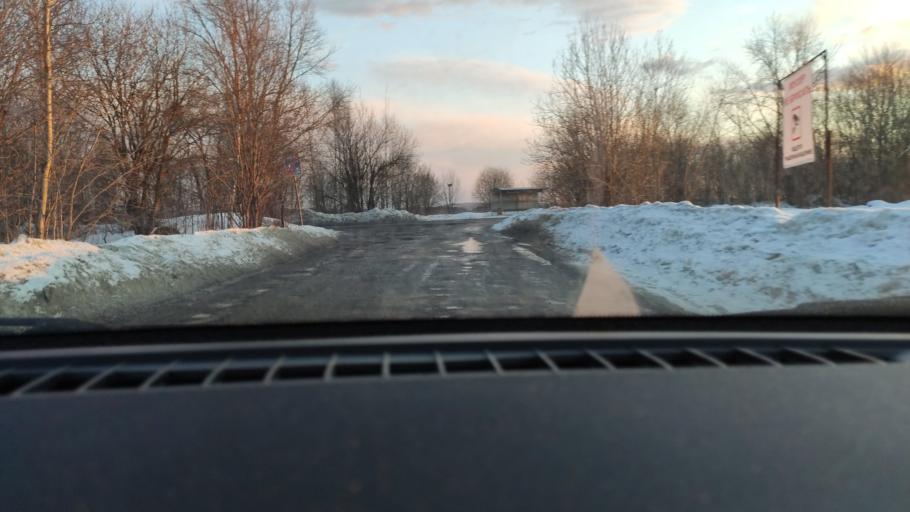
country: RU
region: Perm
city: Perm
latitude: 58.0358
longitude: 56.3711
